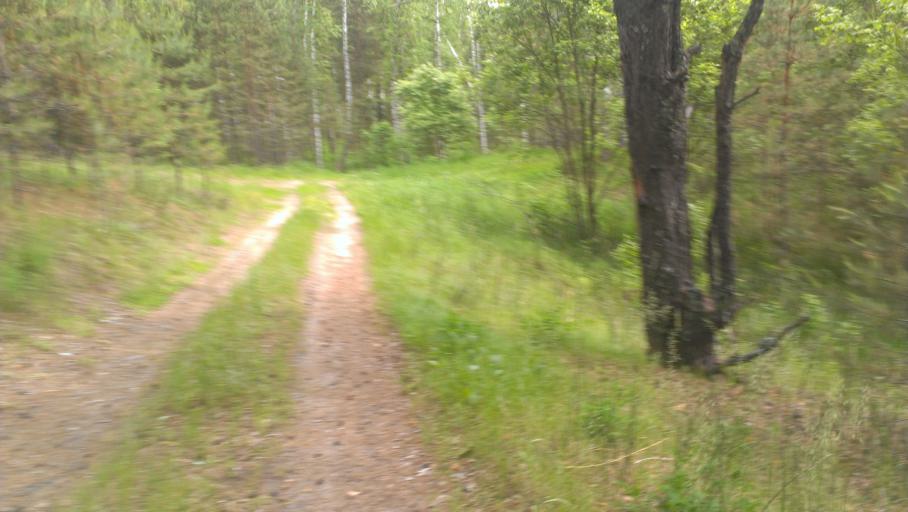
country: RU
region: Altai Krai
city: Sannikovo
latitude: 53.3473
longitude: 84.0402
